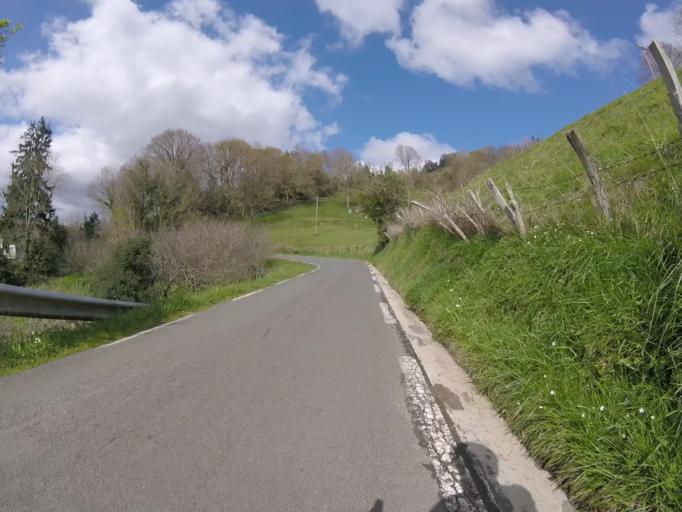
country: ES
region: Basque Country
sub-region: Provincia de Guipuzcoa
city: Tolosa
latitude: 43.1286
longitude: -2.1001
